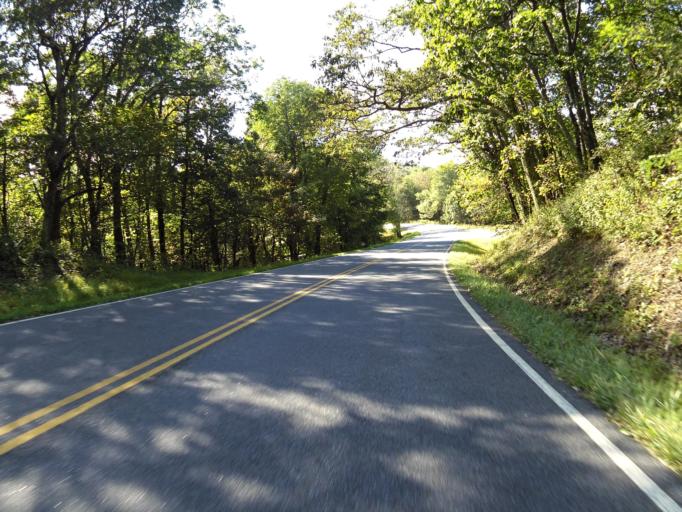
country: US
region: Virginia
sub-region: Page County
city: Stanley
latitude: 38.5334
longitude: -78.4201
